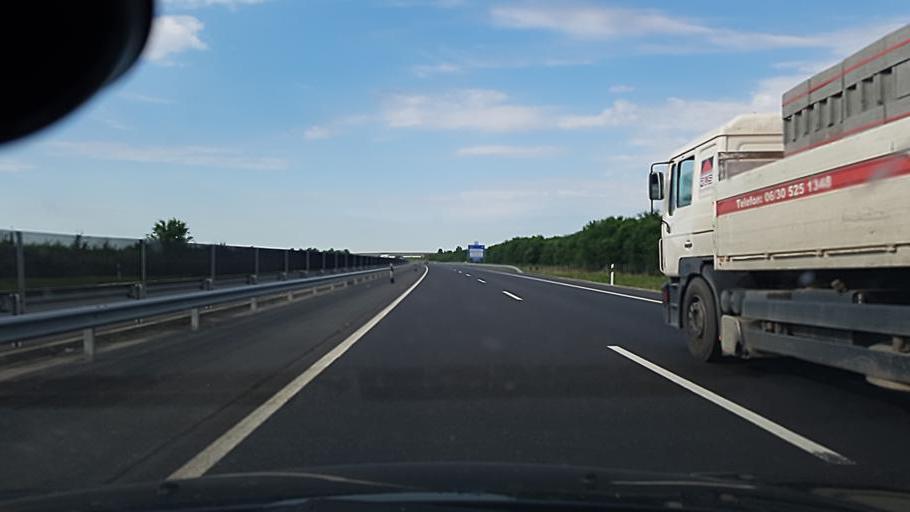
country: HU
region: Pest
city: Szazhalombatta
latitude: 47.3191
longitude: 18.8723
